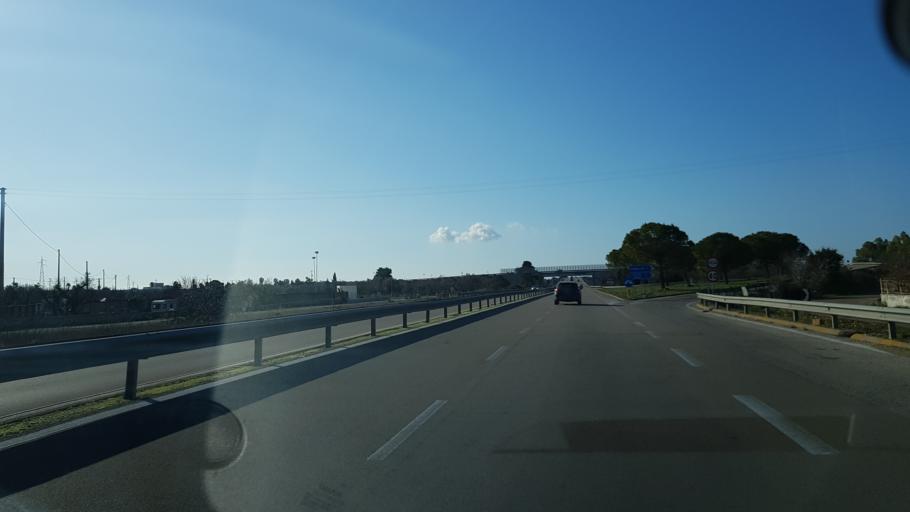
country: IT
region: Apulia
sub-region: Provincia di Lecce
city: Galatone
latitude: 40.1214
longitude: 18.0488
